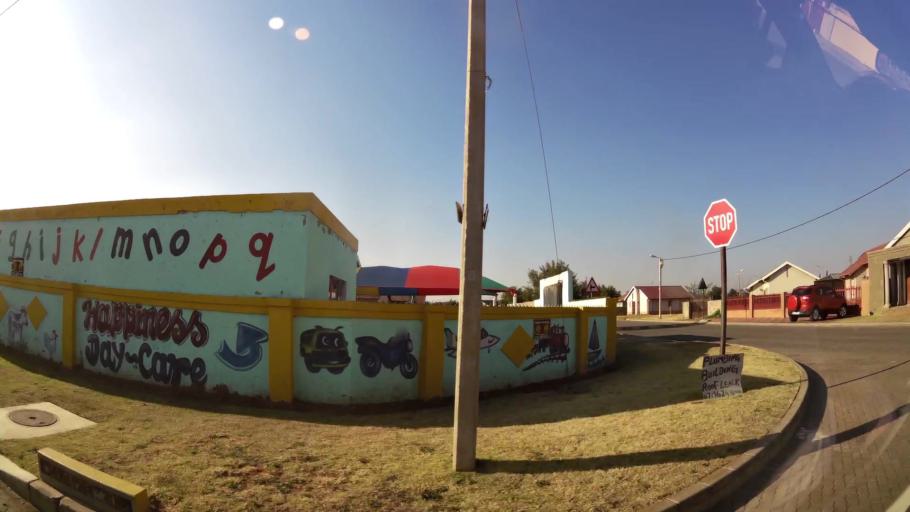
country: ZA
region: Gauteng
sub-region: West Rand District Municipality
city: Randfontein
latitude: -26.1916
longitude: 27.6994
